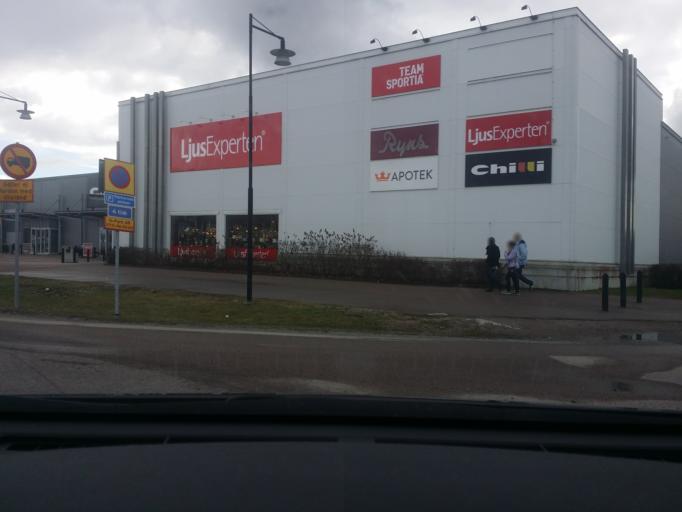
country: SE
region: Vaestmanland
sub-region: Vasteras
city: Vasteras
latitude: 59.6186
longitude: 16.4615
